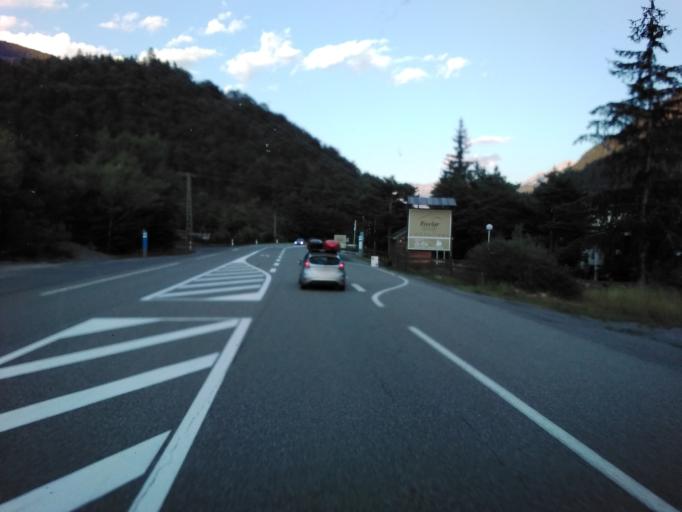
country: FR
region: Provence-Alpes-Cote d'Azur
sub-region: Departement des Alpes-de-Haute-Provence
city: Barcelonnette
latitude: 44.3997
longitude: 6.5308
